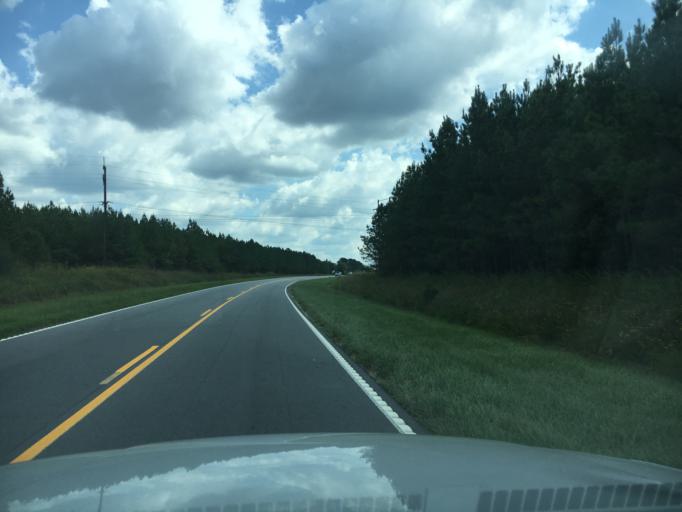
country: US
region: South Carolina
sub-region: Greenwood County
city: Greenwood
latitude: 34.1517
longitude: -82.1613
